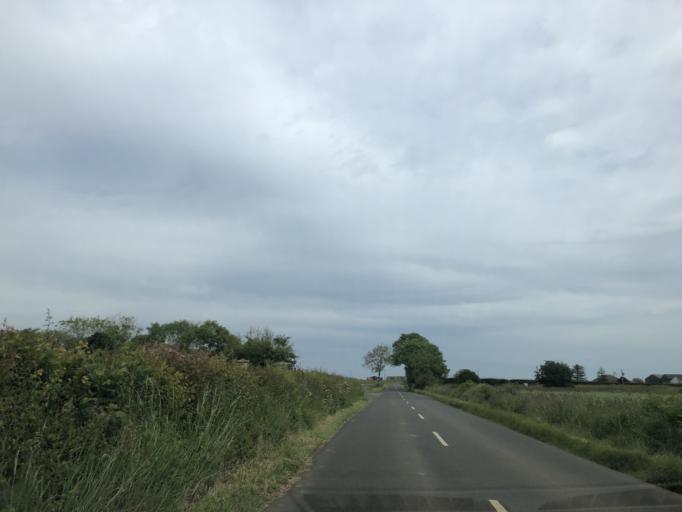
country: GB
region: Scotland
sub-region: Fife
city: Anstruther
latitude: 56.2548
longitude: -2.7015
